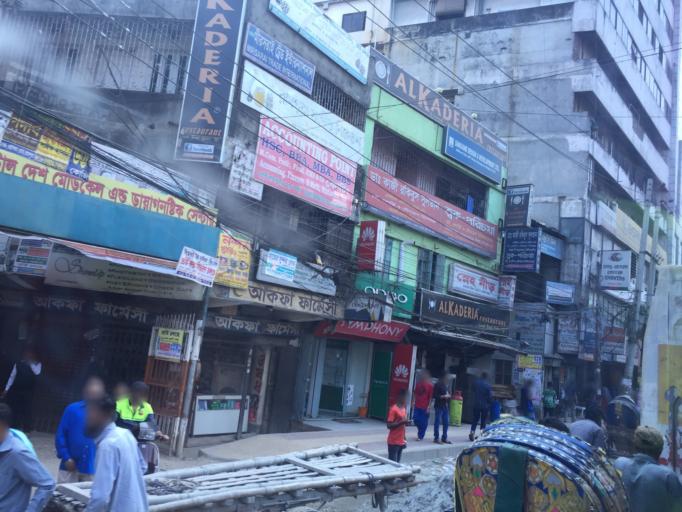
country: BD
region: Dhaka
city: Paltan
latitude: 23.7594
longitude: 90.4185
